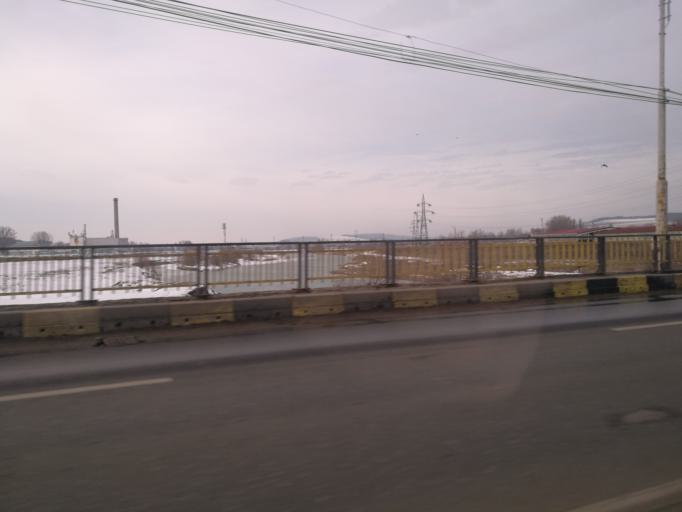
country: RO
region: Suceava
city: Suceava
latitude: 47.6583
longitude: 26.2638
